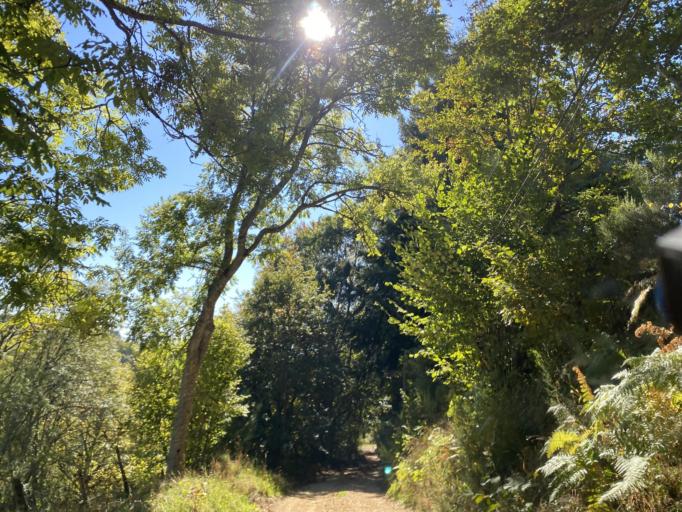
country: FR
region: Rhone-Alpes
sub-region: Departement de la Loire
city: Saint-Just-en-Chevalet
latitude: 45.9596
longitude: 3.8643
